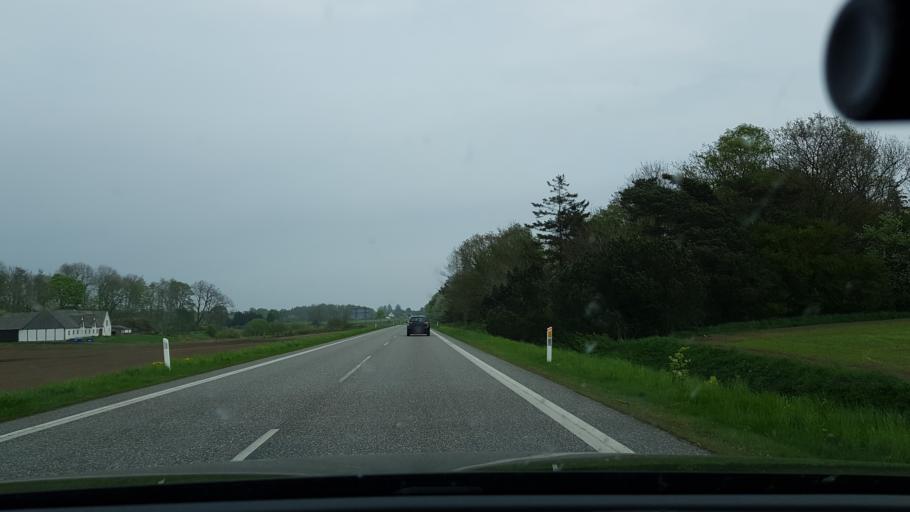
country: DK
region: Capital Region
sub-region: Bornholm Kommune
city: Nexo
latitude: 55.0243
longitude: 15.0974
